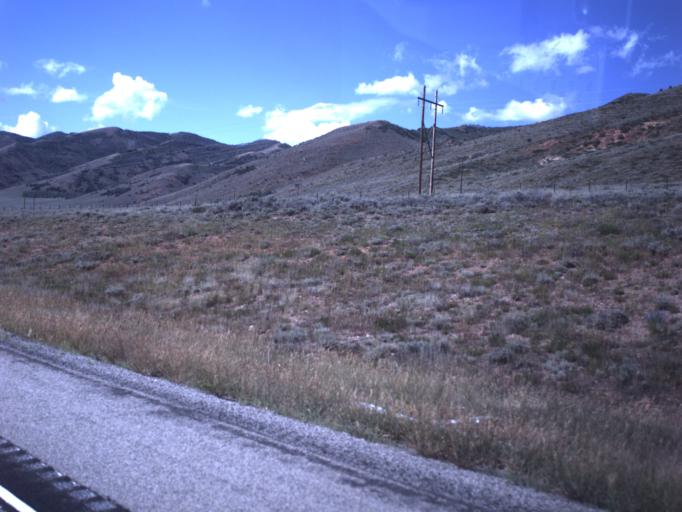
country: US
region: Utah
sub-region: Wasatch County
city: Heber
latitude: 40.2232
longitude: -111.1062
